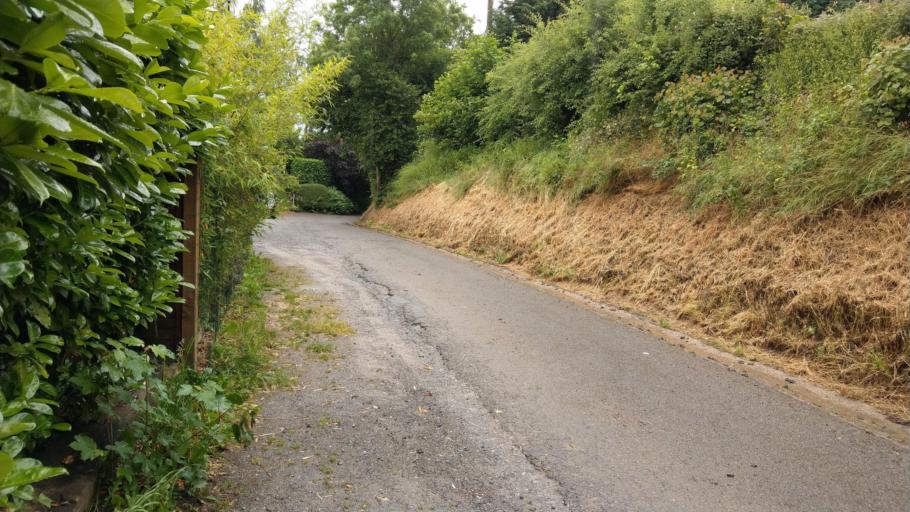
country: NL
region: Limburg
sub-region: Gemeente Vaals
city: Vaals
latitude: 50.7479
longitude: 5.9923
